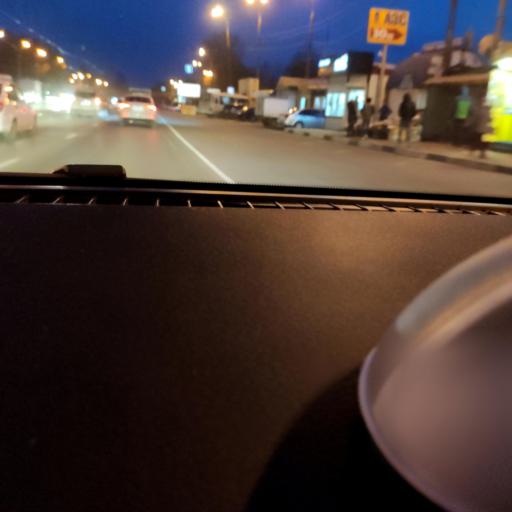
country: RU
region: Samara
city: Smyshlyayevka
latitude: 53.2097
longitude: 50.2744
